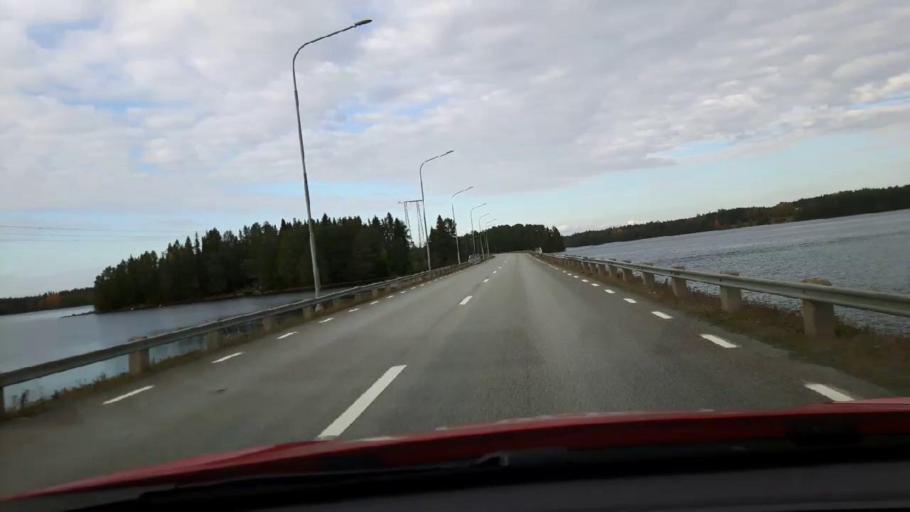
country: SE
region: Jaemtland
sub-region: Krokoms Kommun
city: Valla
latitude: 63.2464
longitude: 13.9994
